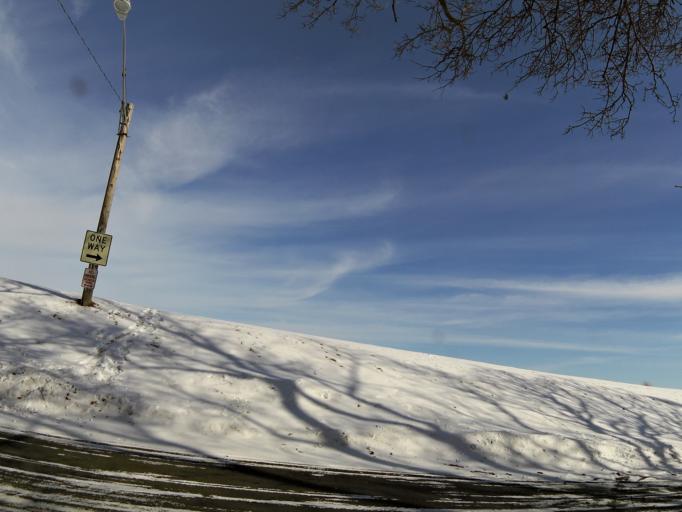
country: US
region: Minnesota
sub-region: Washington County
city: Lake Saint Croix Beach
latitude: 44.9228
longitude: -92.7645
